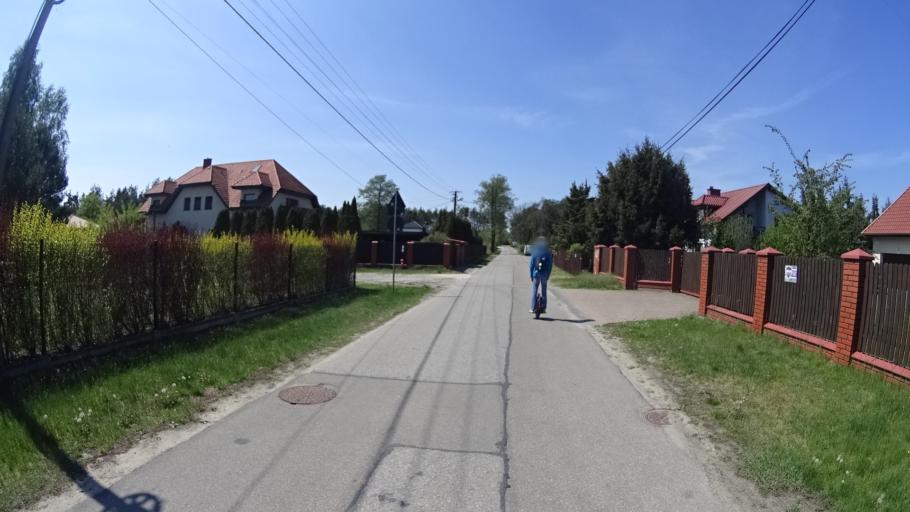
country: PL
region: Masovian Voivodeship
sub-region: Powiat warszawski zachodni
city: Truskaw
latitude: 52.2799
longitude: 20.7482
